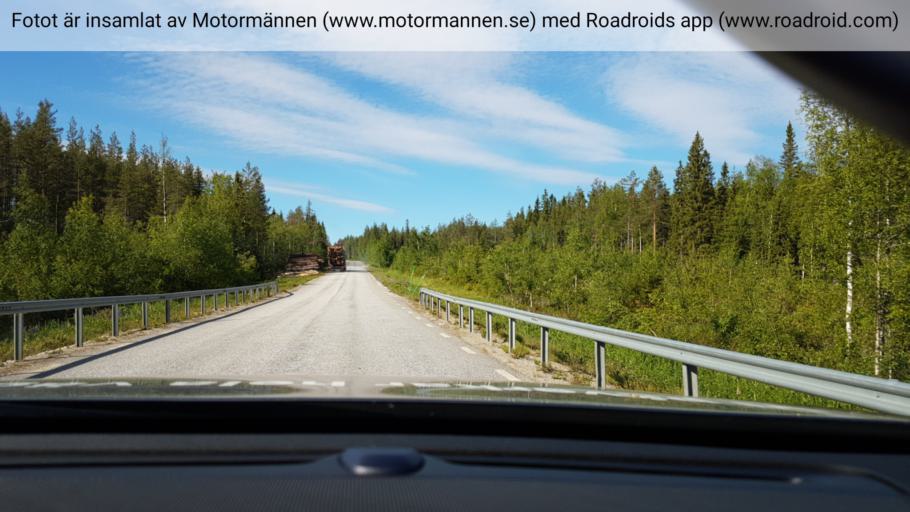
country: SE
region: Vaesterbotten
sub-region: Bjurholms Kommun
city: Bjurholm
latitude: 63.9779
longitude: 19.3230
